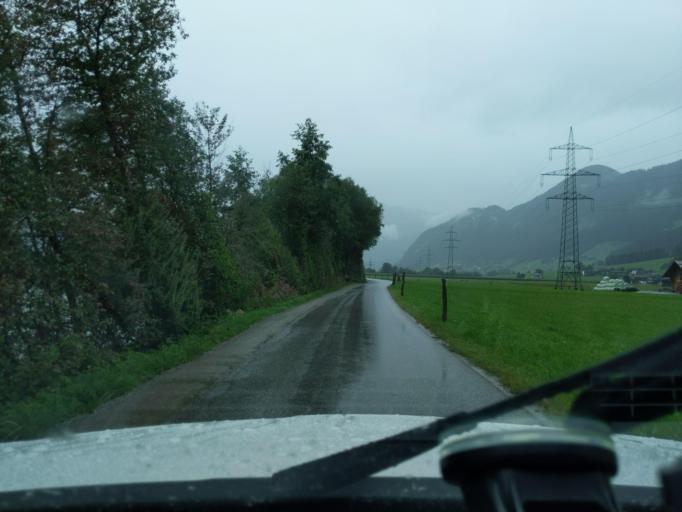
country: AT
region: Tyrol
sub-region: Politischer Bezirk Schwaz
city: Hart im Zillertal
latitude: 47.3621
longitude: 11.8619
